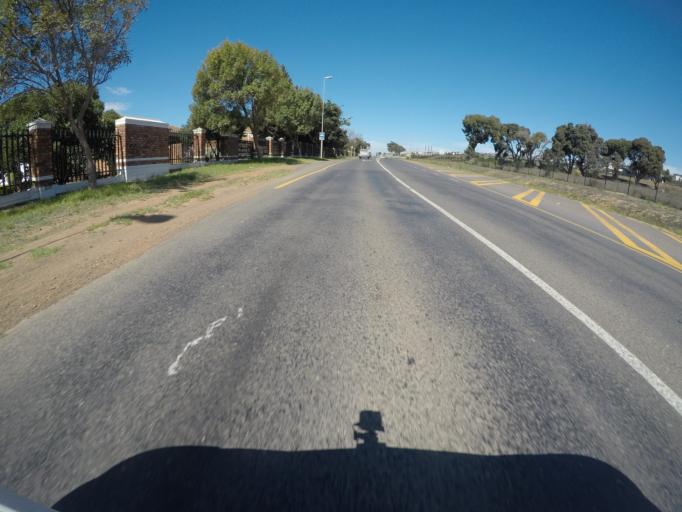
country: ZA
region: Western Cape
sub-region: City of Cape Town
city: Kraaifontein
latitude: -33.8166
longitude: 18.6340
